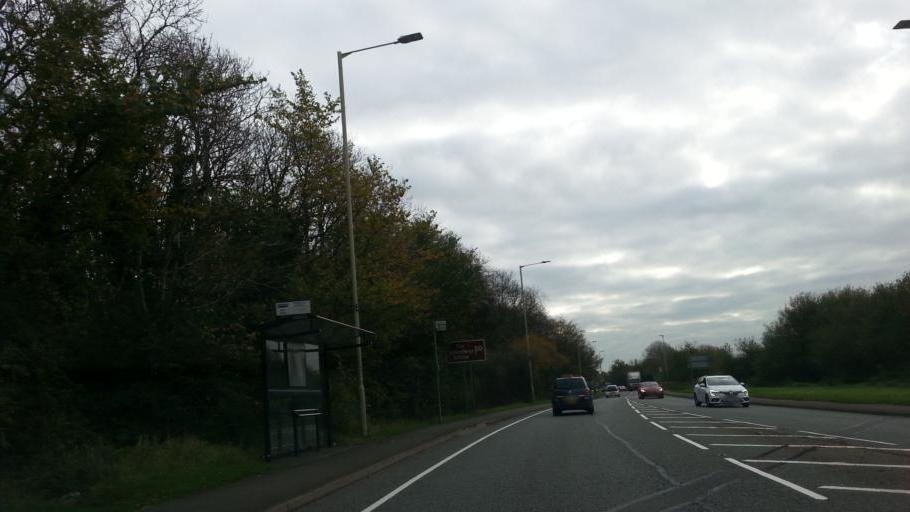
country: GB
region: England
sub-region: Leicestershire
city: Anstey
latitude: 52.6642
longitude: -1.1761
